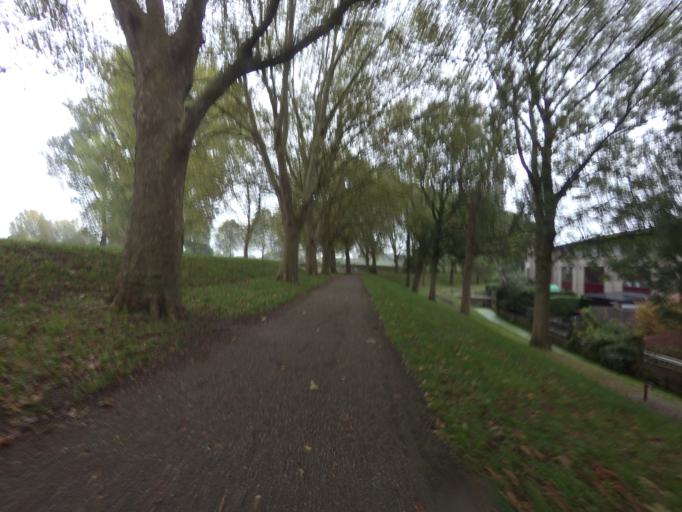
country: NL
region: South Holland
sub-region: Gemeente Gorinchem
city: Gorinchem
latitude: 51.8322
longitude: 4.9811
